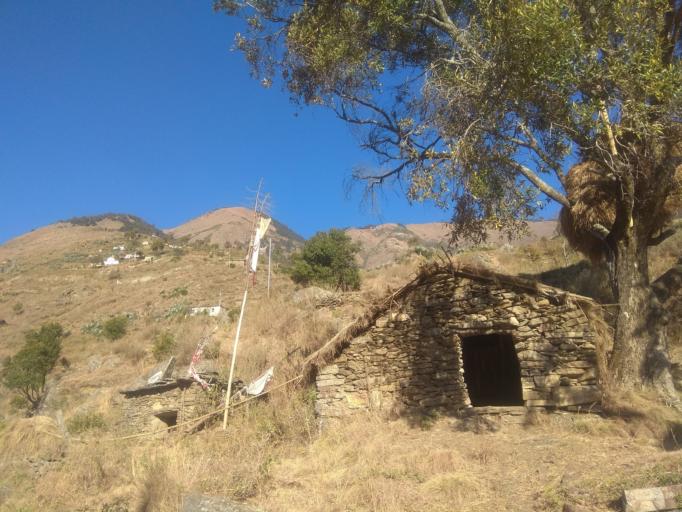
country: NP
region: Mid Western
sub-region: Bheri Zone
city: Dailekh
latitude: 29.2871
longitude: 81.7132
